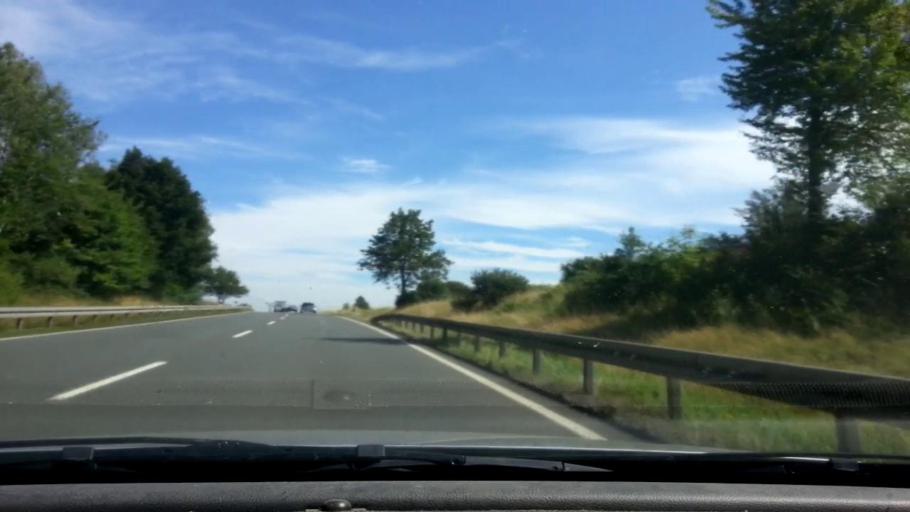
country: DE
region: Bavaria
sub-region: Upper Franconia
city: Marktredwitz
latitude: 50.0183
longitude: 12.1249
